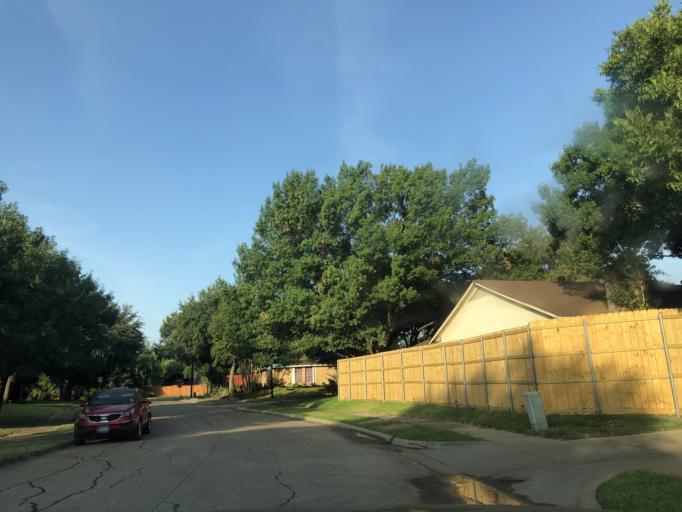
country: US
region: Texas
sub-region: Dallas County
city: Garland
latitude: 32.8547
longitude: -96.6256
